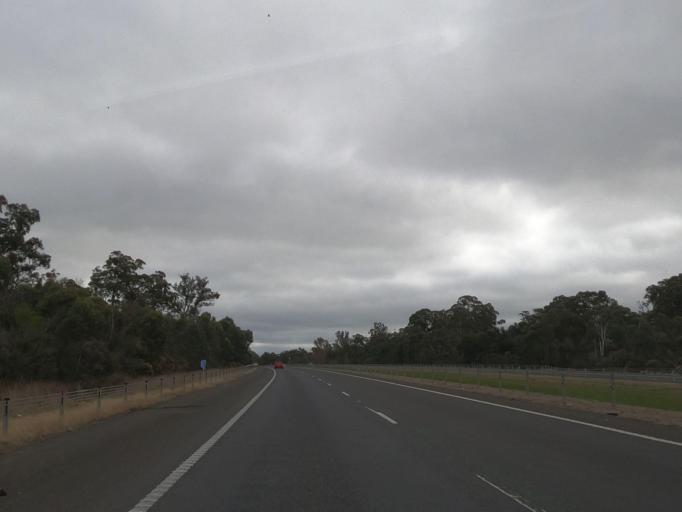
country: AU
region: Victoria
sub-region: Mount Alexander
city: Castlemaine
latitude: -37.0988
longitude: 144.3638
